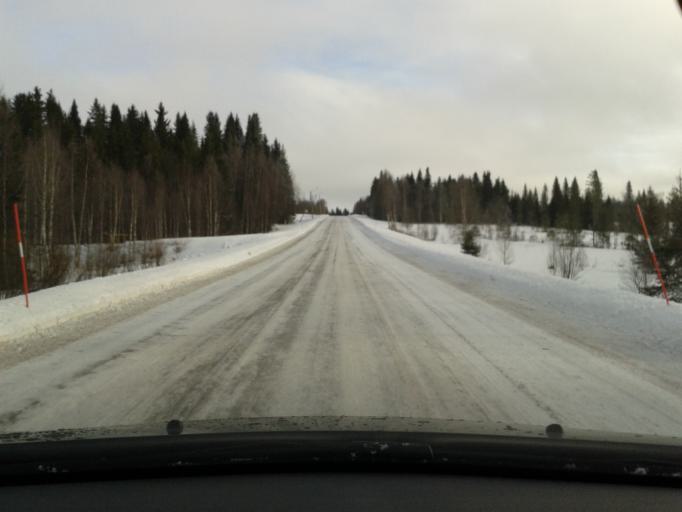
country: SE
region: Vaesterbotten
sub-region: Vilhelmina Kommun
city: Sjoberg
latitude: 64.7953
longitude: 16.0631
